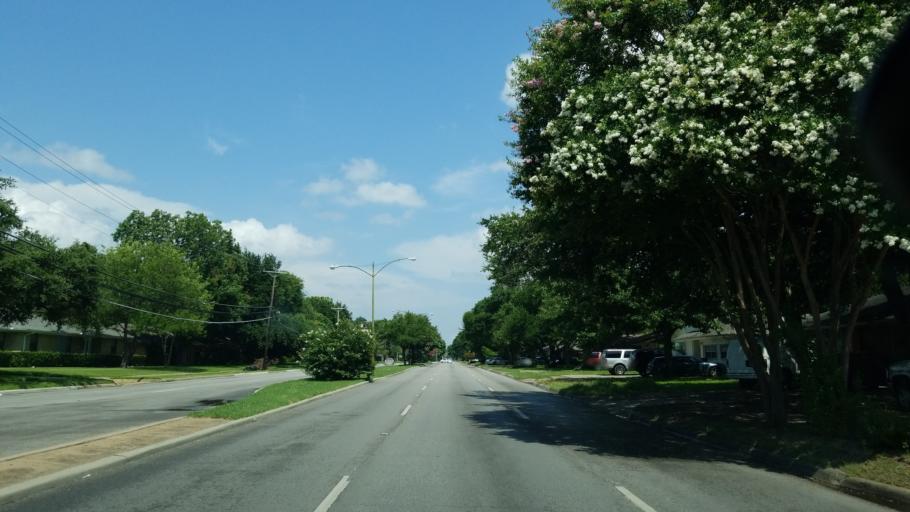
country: US
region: Texas
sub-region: Dallas County
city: Farmers Branch
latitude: 32.8809
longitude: -96.8715
